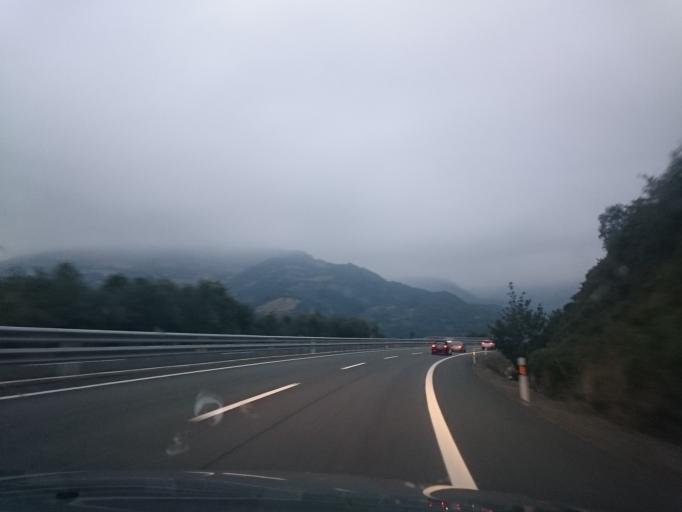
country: ES
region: Asturias
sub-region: Province of Asturias
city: Pola de Lena
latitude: 43.0573
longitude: -5.8241
